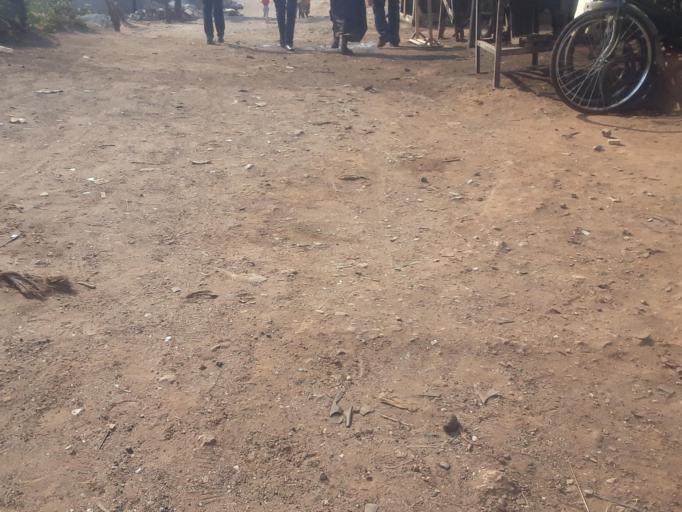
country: ZM
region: Lusaka
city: Lusaka
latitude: -15.3611
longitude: 28.2980
